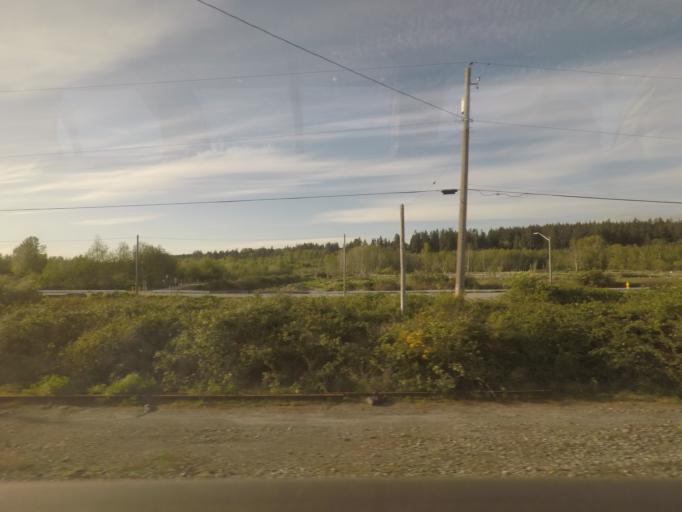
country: CA
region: British Columbia
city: Delta
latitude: 49.0934
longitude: -122.8843
